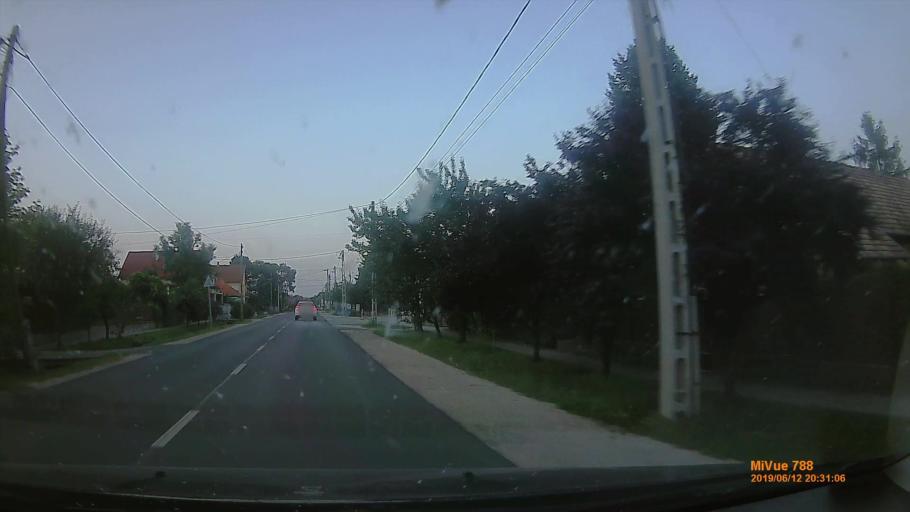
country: HU
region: Pest
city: Vecses
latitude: 47.4023
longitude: 19.2518
